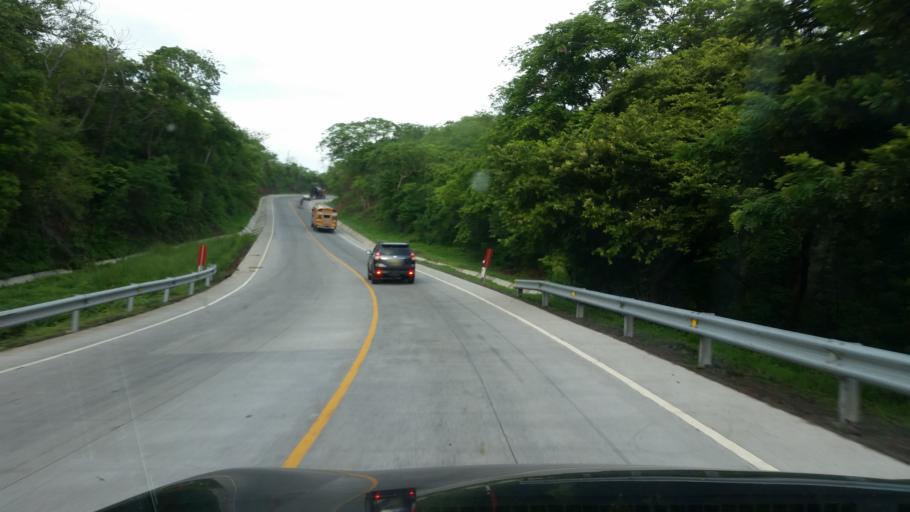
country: NI
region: Managua
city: Carlos Fonseca Amador
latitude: 12.0655
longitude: -86.4495
